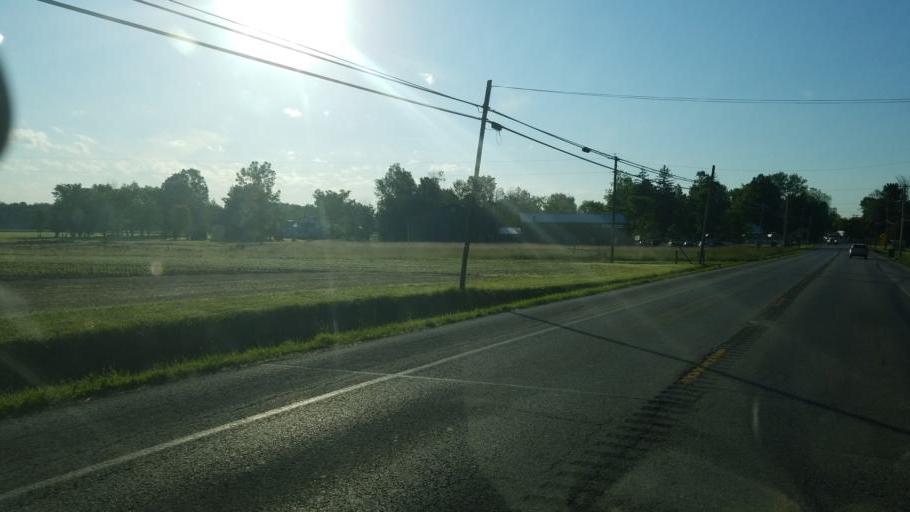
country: US
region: Ohio
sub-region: Wayne County
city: Wooster
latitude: 40.7653
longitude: -81.9005
